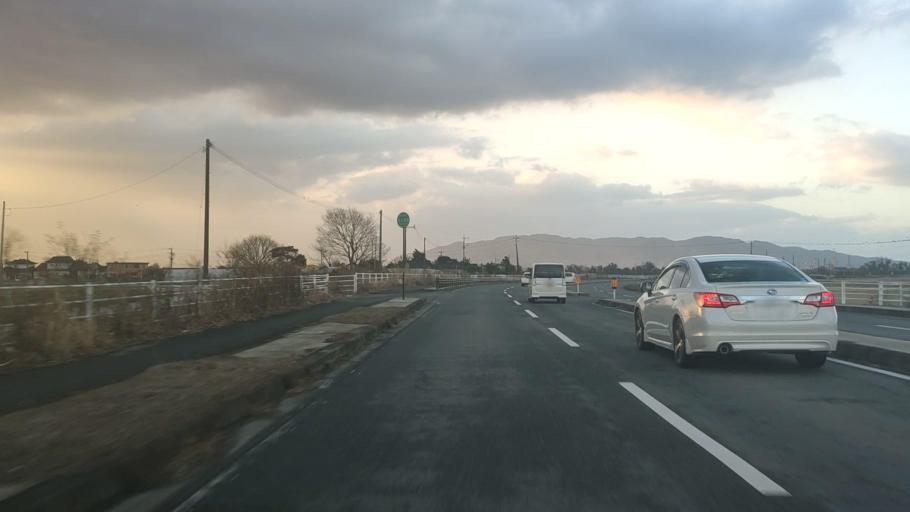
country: JP
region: Kumamoto
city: Kumamoto
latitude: 32.7488
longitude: 130.7070
